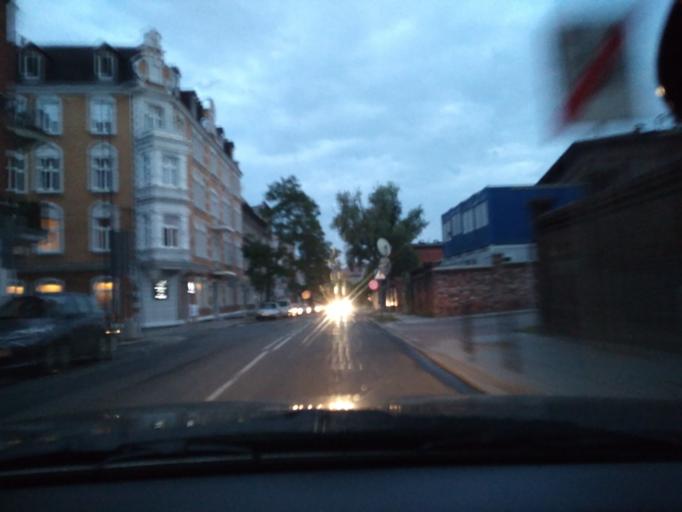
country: PL
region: Silesian Voivodeship
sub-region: Gliwice
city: Gliwice
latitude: 50.2901
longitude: 18.6574
